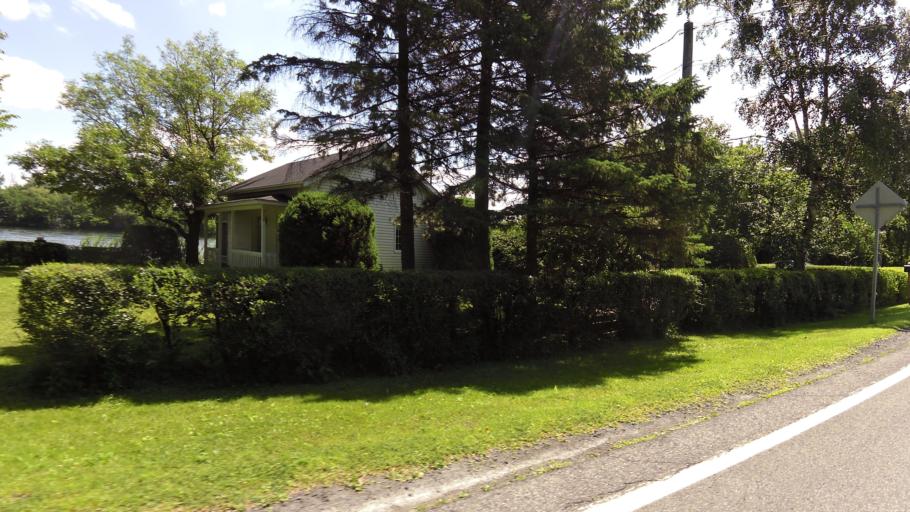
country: CA
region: Quebec
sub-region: Monteregie
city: Richelieu
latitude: 45.4284
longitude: -73.2490
